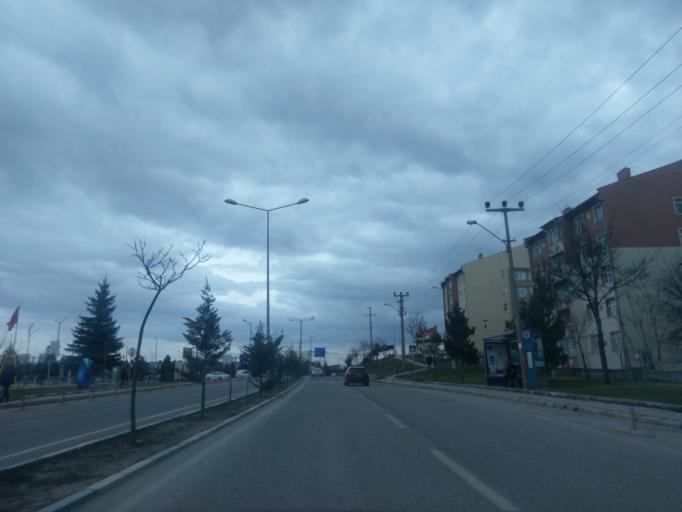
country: TR
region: Kuetahya
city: Kutahya
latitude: 39.3912
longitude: 30.0345
